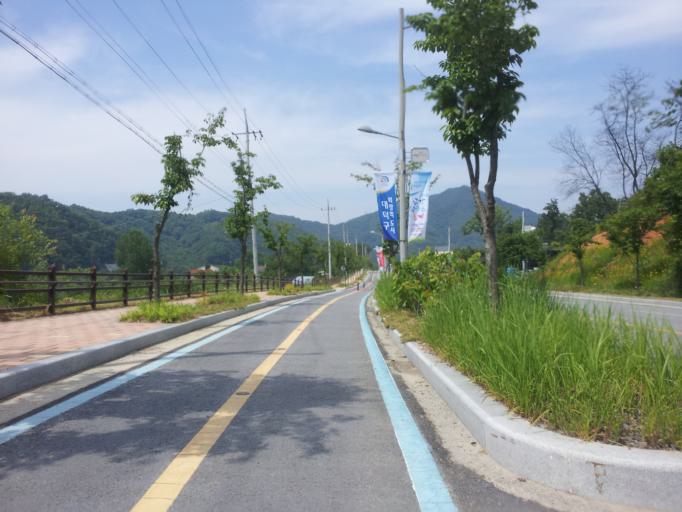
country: KR
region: Daejeon
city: Sintansin
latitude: 36.4614
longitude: 127.4661
